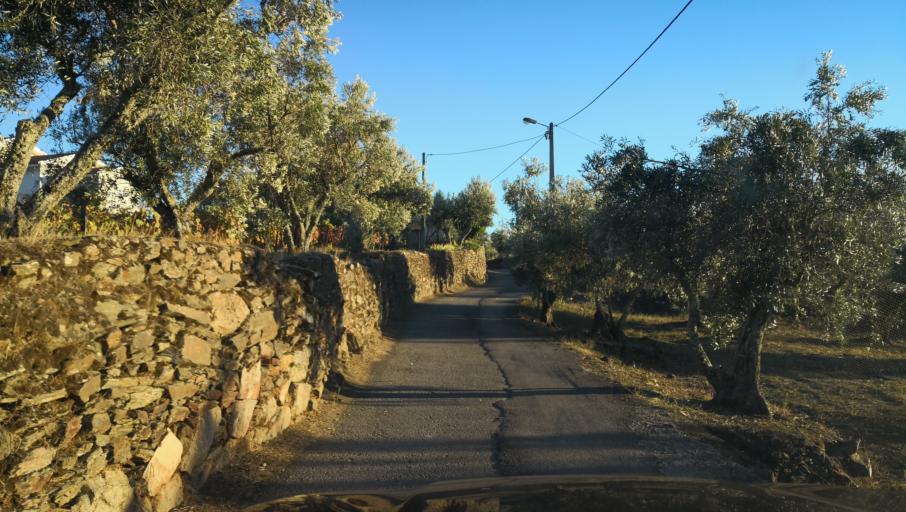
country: PT
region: Vila Real
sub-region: Santa Marta de Penaguiao
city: Santa Marta de Penaguiao
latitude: 41.2473
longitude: -7.7669
